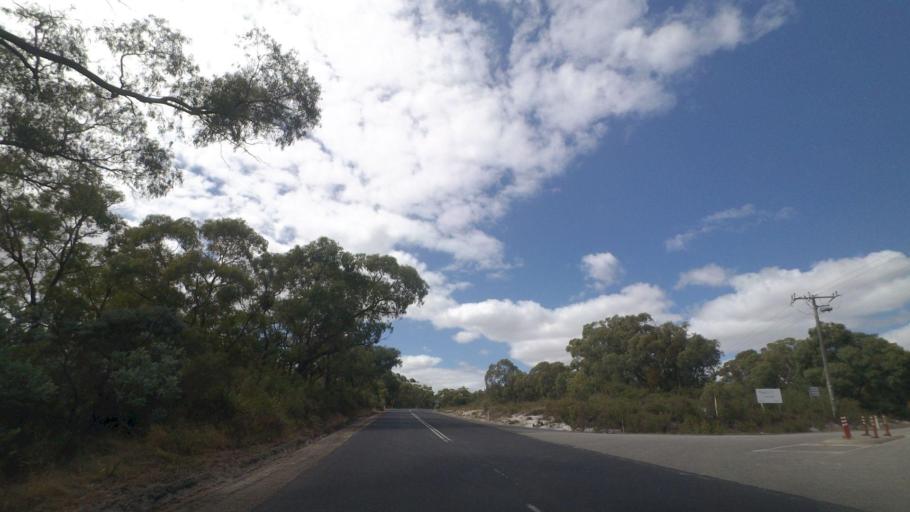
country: AU
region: Victoria
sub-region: Cardinia
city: Koo-Wee-Rup
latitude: -38.2966
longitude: 145.6299
